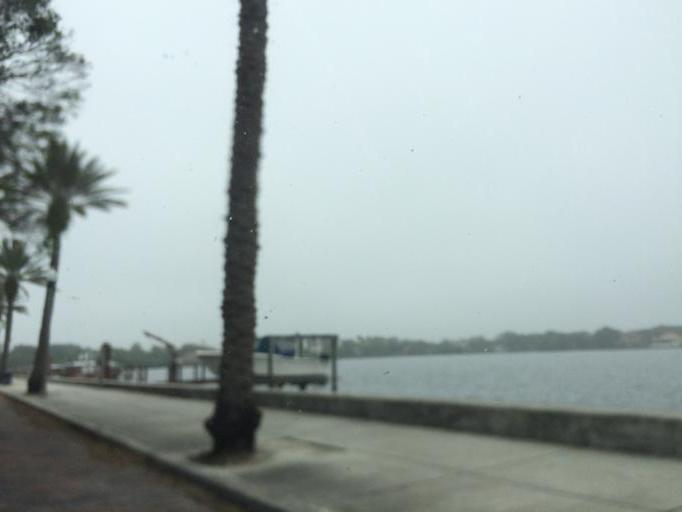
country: US
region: Florida
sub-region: Pinellas County
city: Lealman
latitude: 27.7971
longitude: -82.6332
